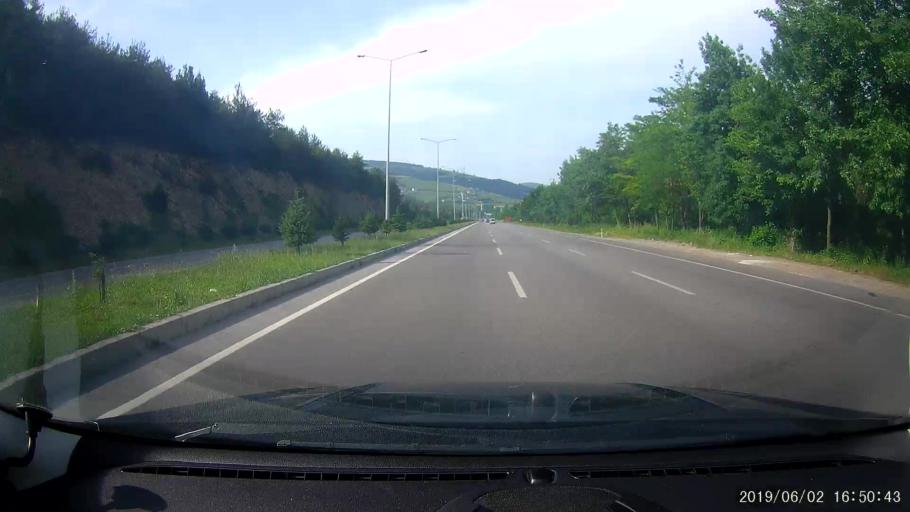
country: TR
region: Samsun
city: Taflan
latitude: 41.2605
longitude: 36.1749
